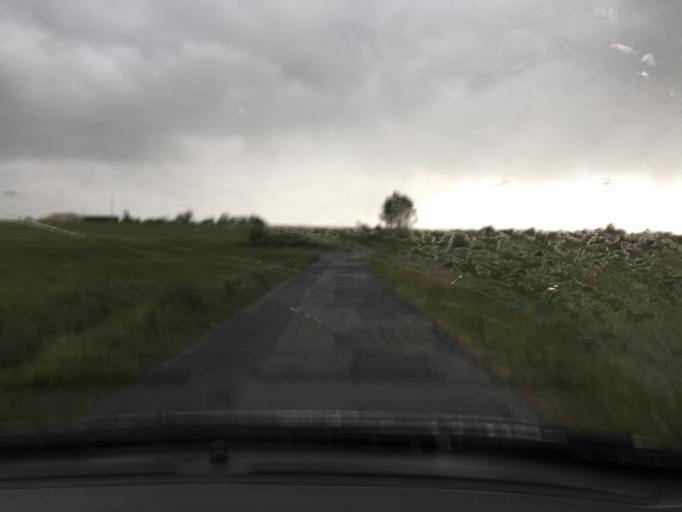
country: FR
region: Rhone-Alpes
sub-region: Departement du Rhone
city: Chassagny
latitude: 45.6138
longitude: 4.7298
